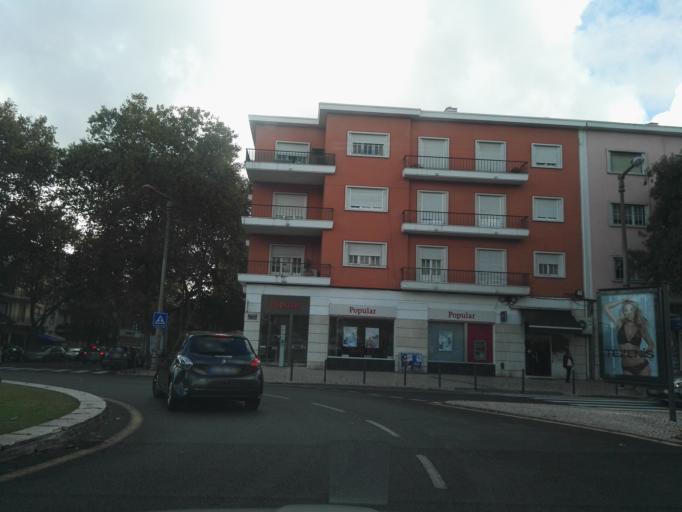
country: PT
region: Lisbon
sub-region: Lisbon
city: Lisbon
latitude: 38.7549
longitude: -9.1389
